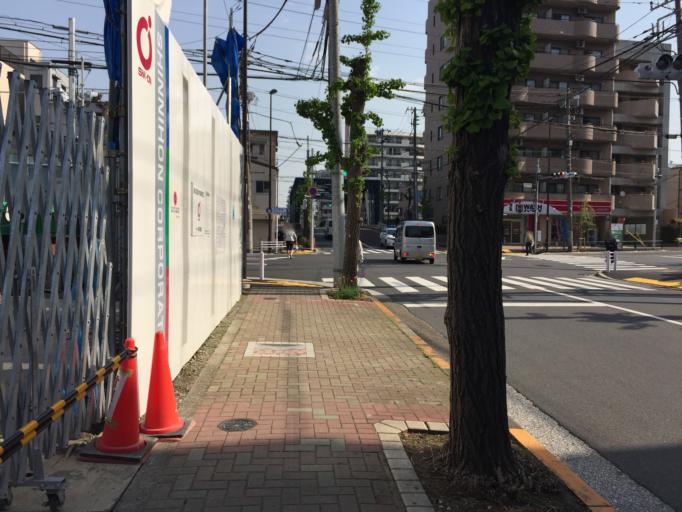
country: JP
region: Tokyo
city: Urayasu
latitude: 35.6750
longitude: 139.8026
